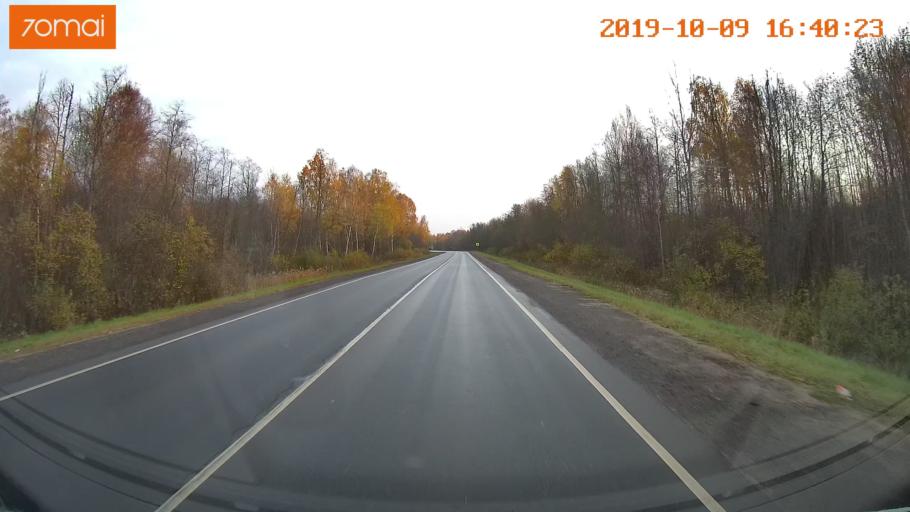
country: RU
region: Kostroma
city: Volgorechensk
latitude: 57.4844
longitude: 41.0601
